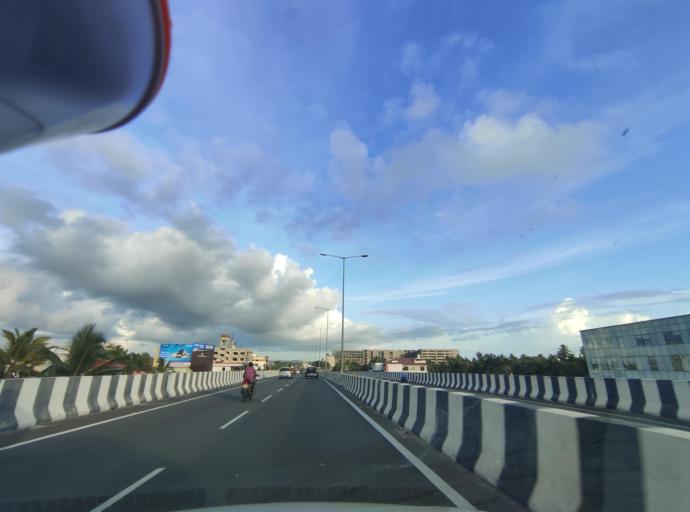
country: IN
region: Kerala
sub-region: Thiruvananthapuram
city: Thiruvananthapuram
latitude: 8.4864
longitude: 76.9271
